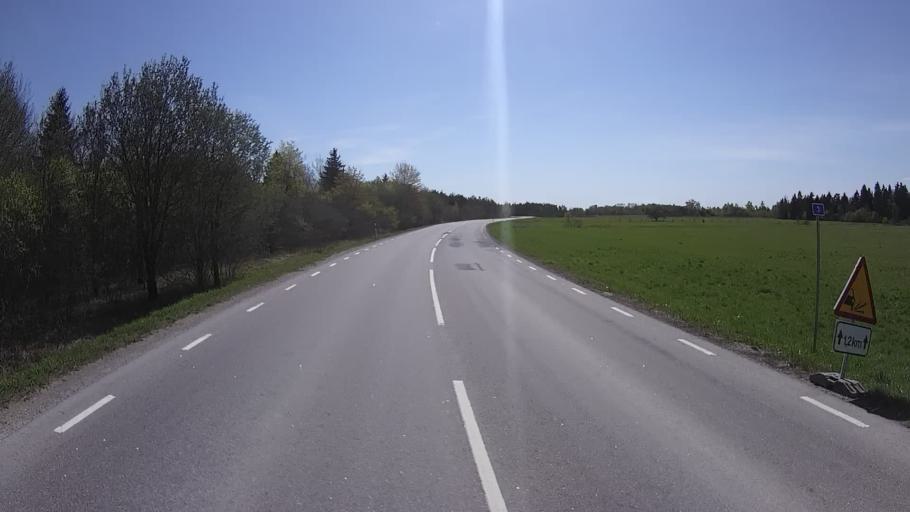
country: EE
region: Harju
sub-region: Keila linn
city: Keila
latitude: 59.3040
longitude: 24.3250
